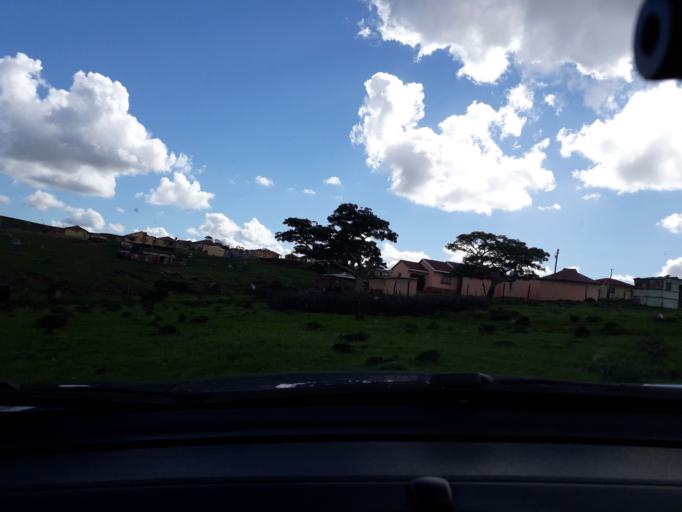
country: ZA
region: Eastern Cape
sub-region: Buffalo City Metropolitan Municipality
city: Bhisho
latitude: -33.1180
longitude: 27.4327
